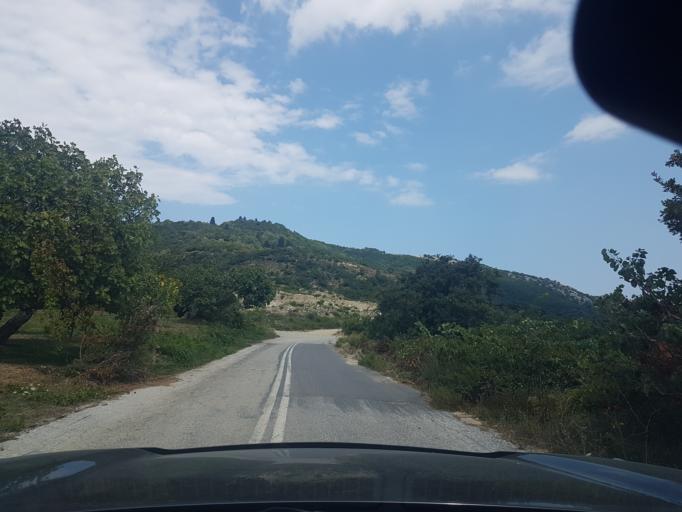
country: GR
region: Central Greece
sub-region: Nomos Evvoias
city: Kymi
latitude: 38.6444
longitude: 24.0534
